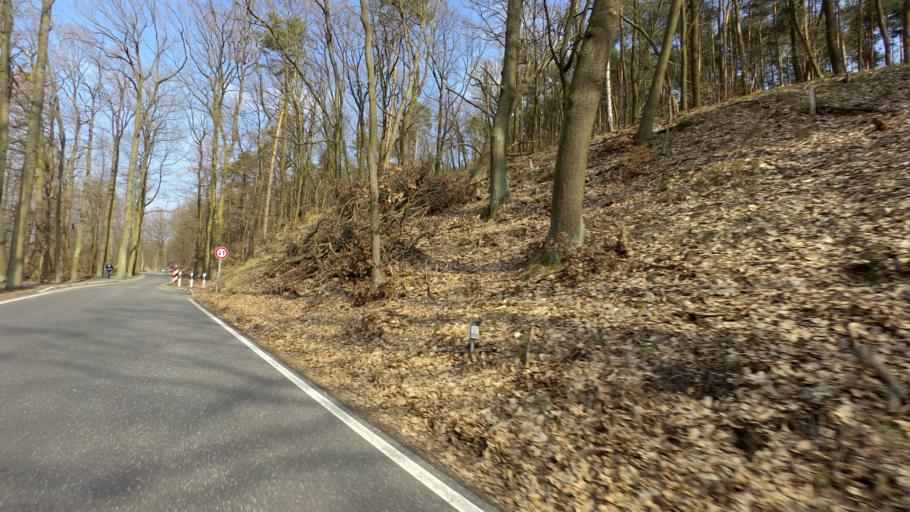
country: DE
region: Brandenburg
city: Werder
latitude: 52.3194
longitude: 12.9523
